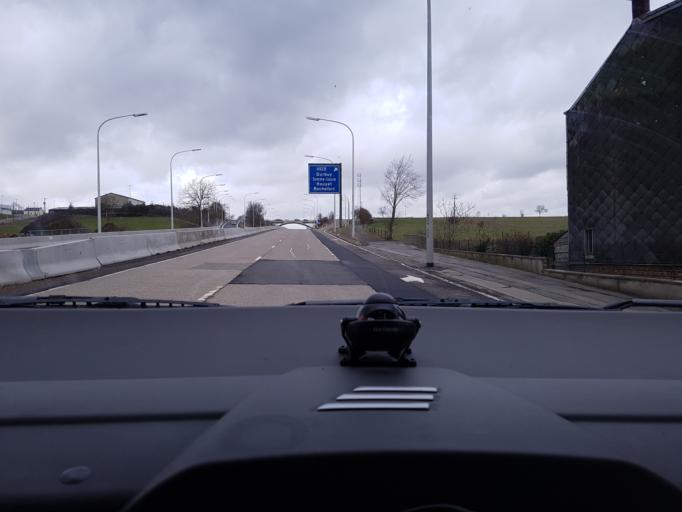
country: BE
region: Wallonia
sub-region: Province de Namur
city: Hamois
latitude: 50.2730
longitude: 5.2394
